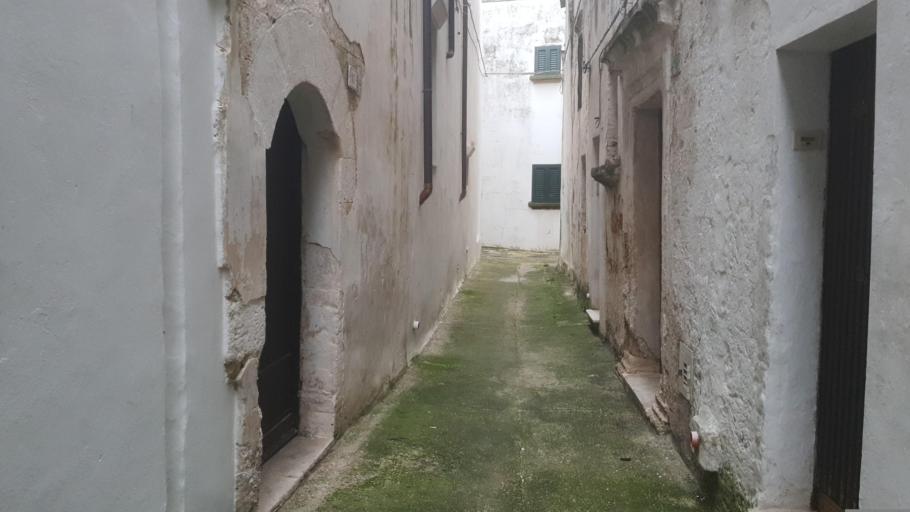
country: IT
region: Apulia
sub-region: Provincia di Lecce
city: Tricase
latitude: 39.9320
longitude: 18.3609
